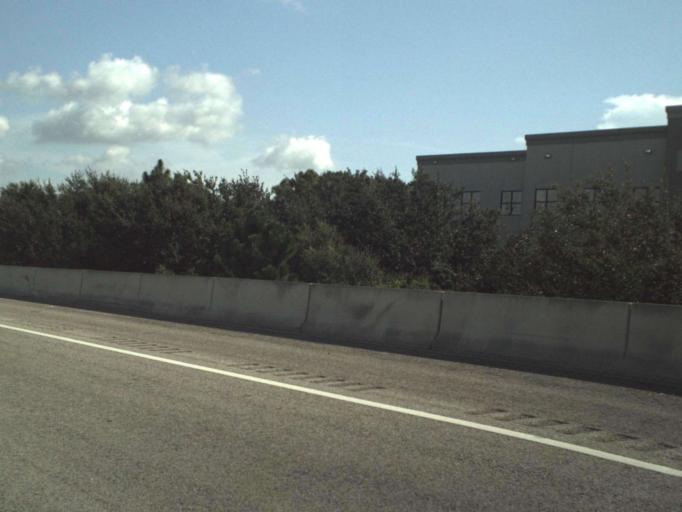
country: US
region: Florida
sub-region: Palm Beach County
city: North Palm Beach
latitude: 26.8326
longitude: -80.0976
